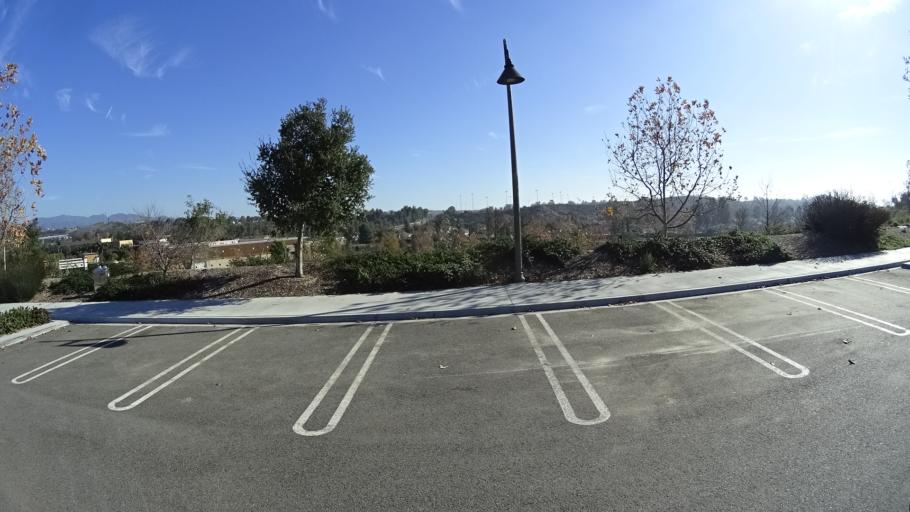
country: US
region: California
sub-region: Orange County
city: Foothill Ranch
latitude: 33.6616
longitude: -117.6561
